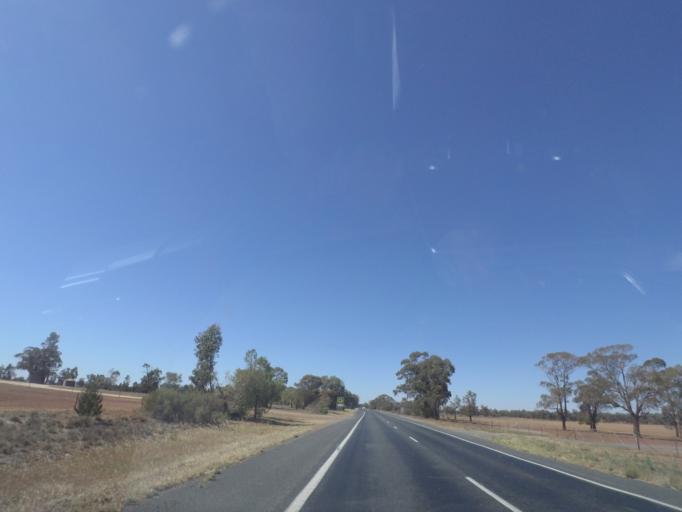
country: AU
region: New South Wales
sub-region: Bland
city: West Wyalong
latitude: -34.1912
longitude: 147.1116
